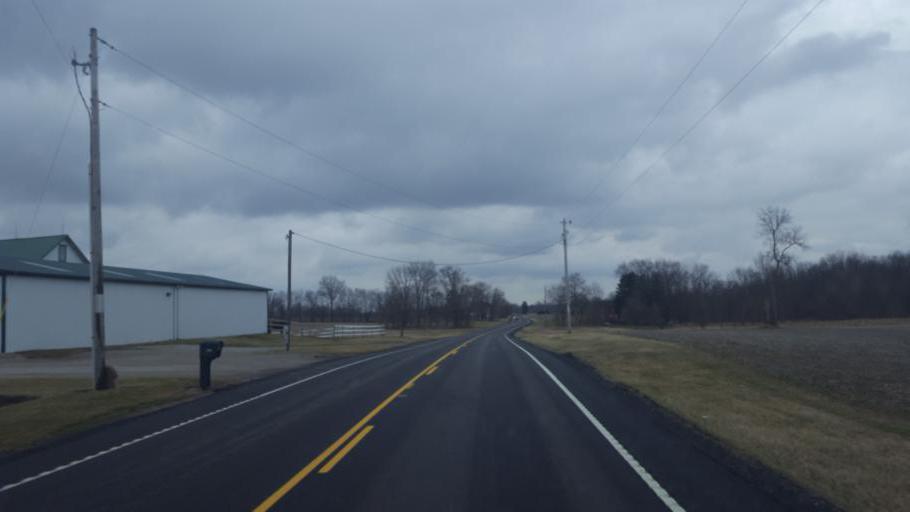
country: US
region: Ohio
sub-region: Knox County
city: Fredericktown
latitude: 40.4700
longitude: -82.5928
